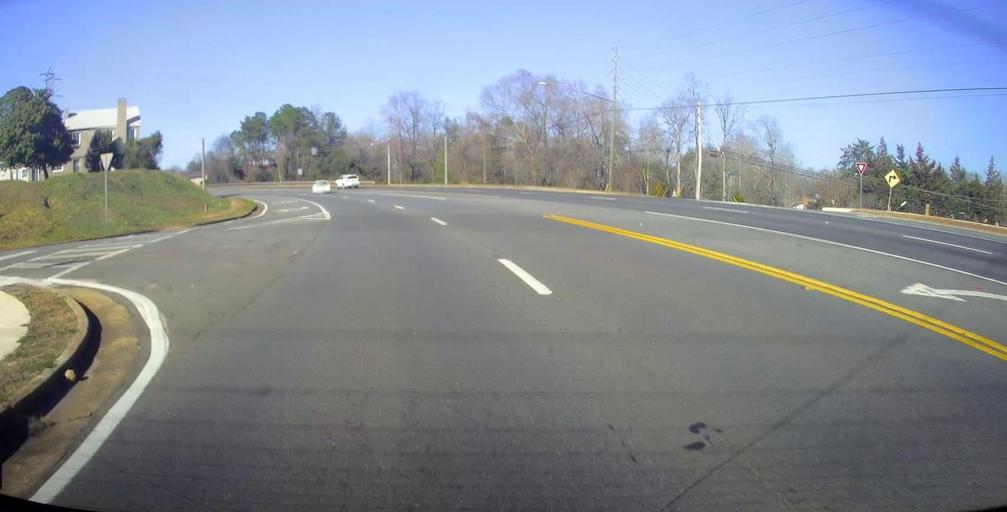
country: US
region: Georgia
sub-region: Sumter County
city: Americus
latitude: 32.0795
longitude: -84.2385
